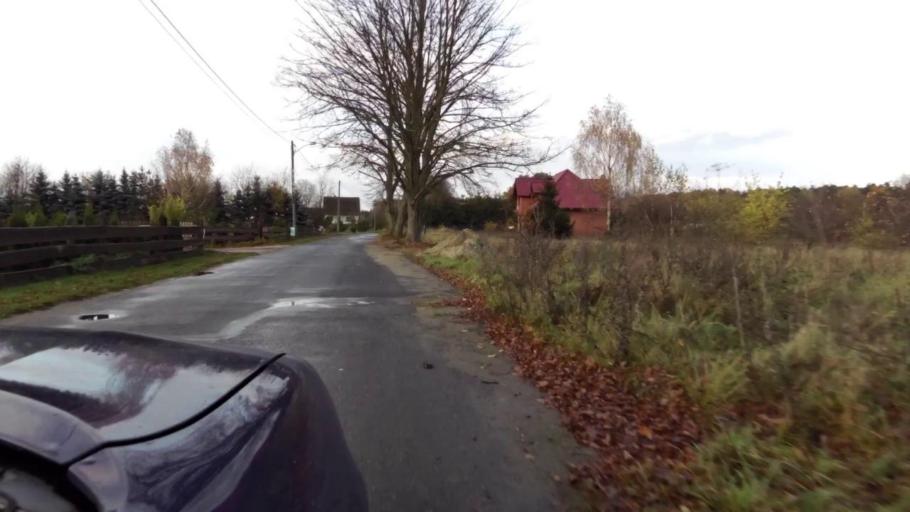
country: PL
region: West Pomeranian Voivodeship
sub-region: Powiat goleniowski
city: Goleniow
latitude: 53.6013
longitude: 14.7547
